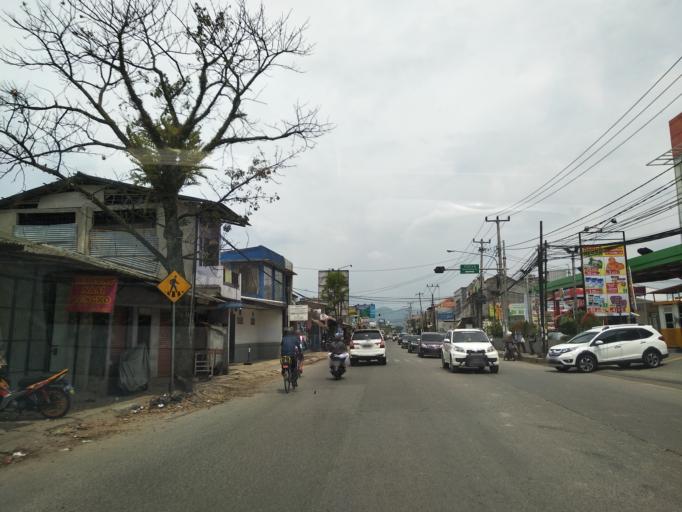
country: ID
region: West Java
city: Pameungpeuk
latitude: -6.9679
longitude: 107.6374
